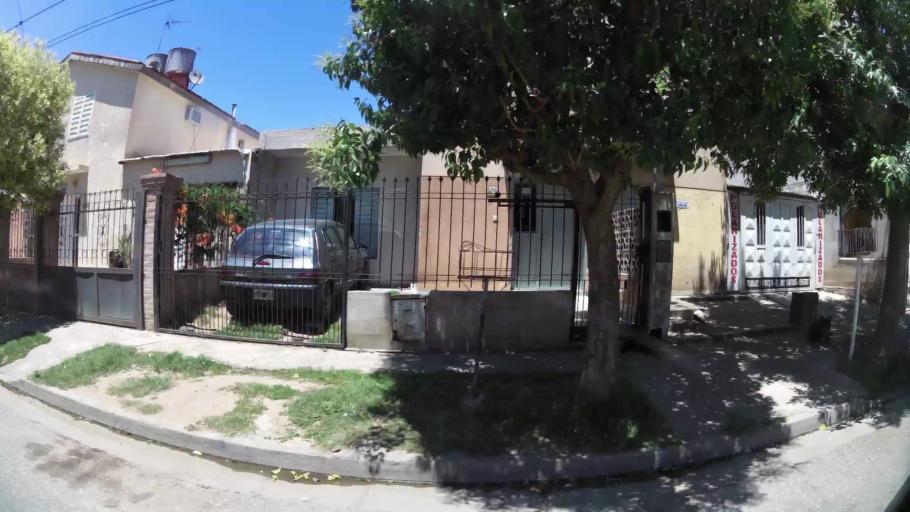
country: AR
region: Cordoba
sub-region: Departamento de Capital
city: Cordoba
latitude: -31.3749
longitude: -64.1306
